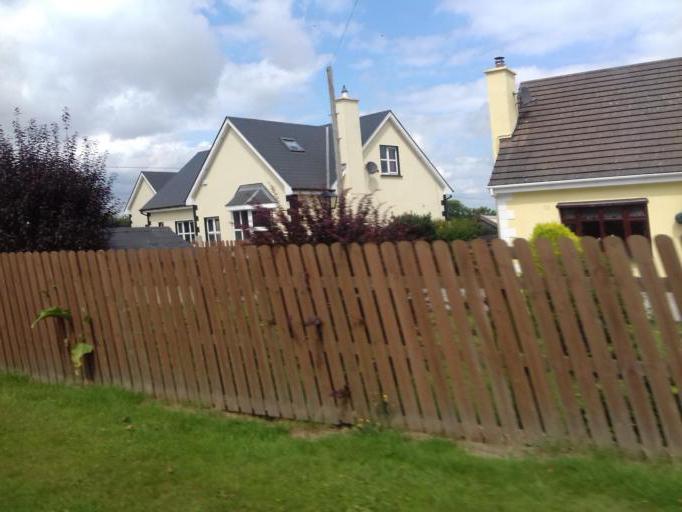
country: IE
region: Leinster
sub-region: Loch Garman
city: Enniscorthy
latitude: 52.4909
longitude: -6.5025
